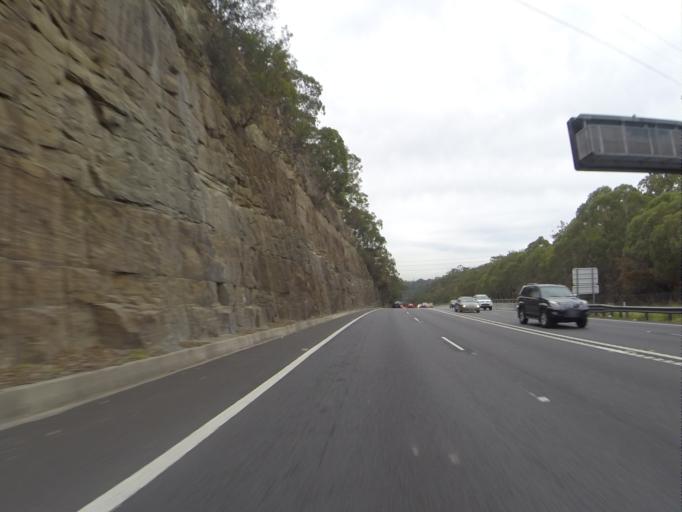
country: AU
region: New South Wales
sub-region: Hurstville
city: Lugarno
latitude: -33.9785
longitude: 151.0302
